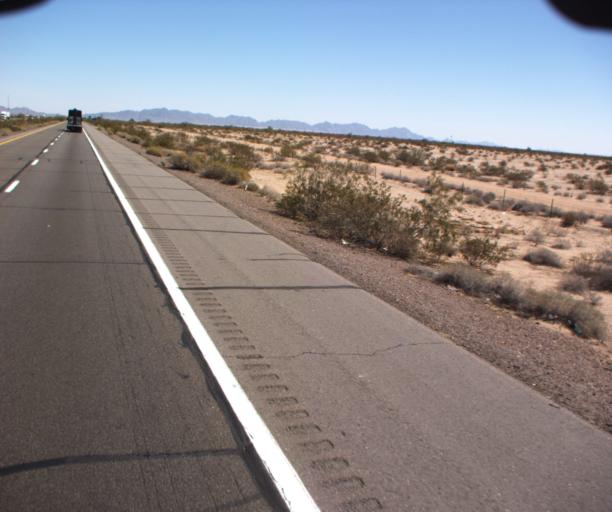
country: US
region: Arizona
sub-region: Yuma County
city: Wellton
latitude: 32.6888
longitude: -113.9834
